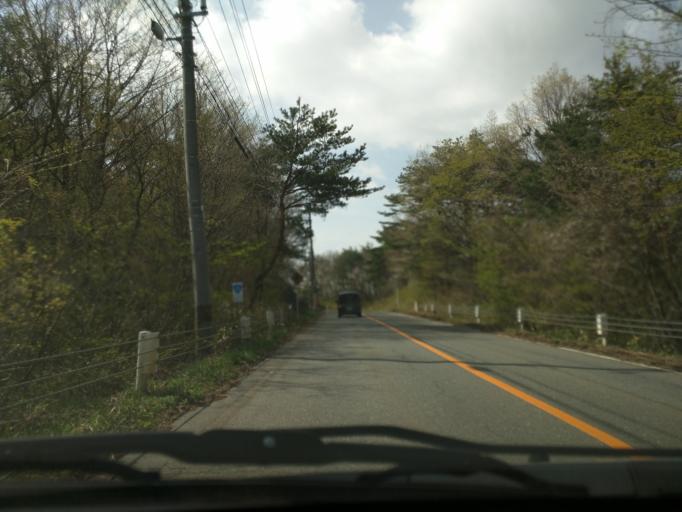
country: JP
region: Fukushima
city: Nihommatsu
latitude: 37.5981
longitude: 140.3623
